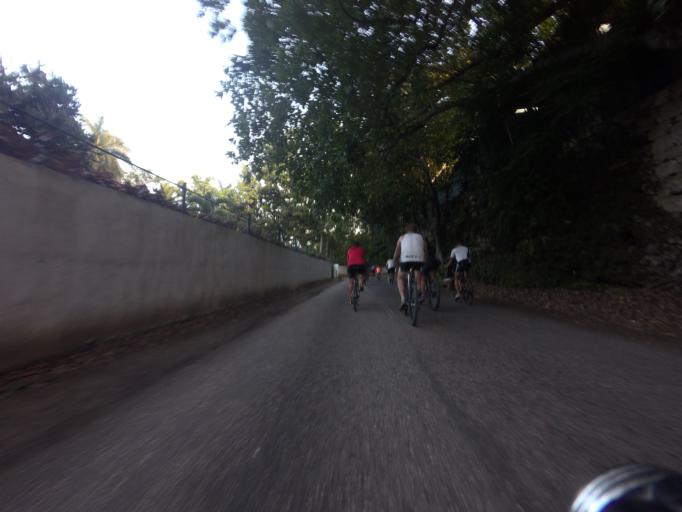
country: CU
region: La Habana
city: Havana
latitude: 23.1171
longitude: -82.4073
